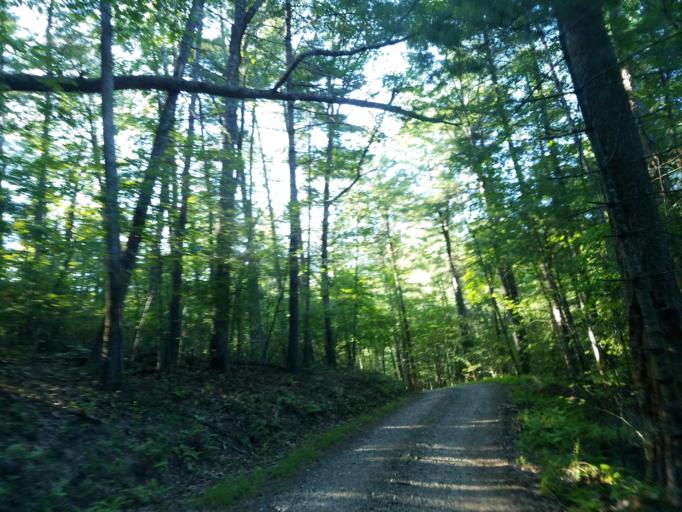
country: US
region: Georgia
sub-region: Union County
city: Blairsville
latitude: 34.7594
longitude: -84.1177
